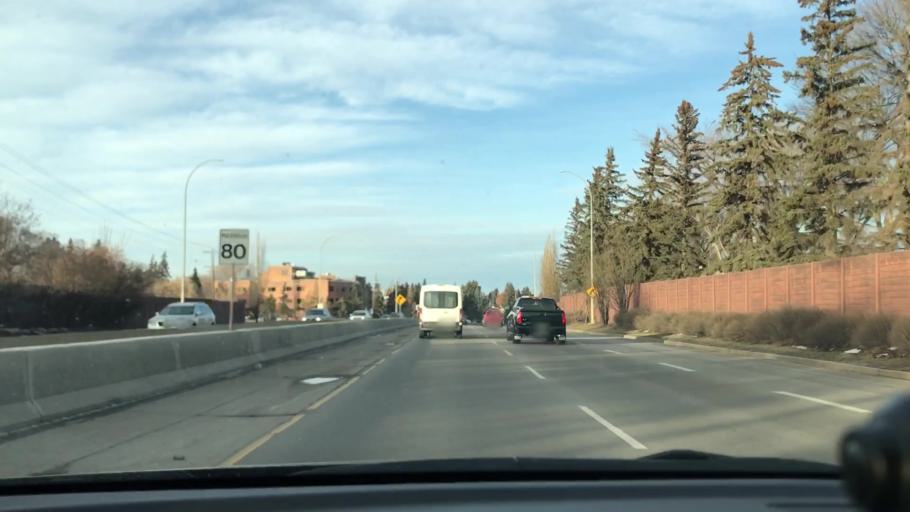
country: CA
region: Alberta
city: Edmonton
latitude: 53.5433
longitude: -113.4434
